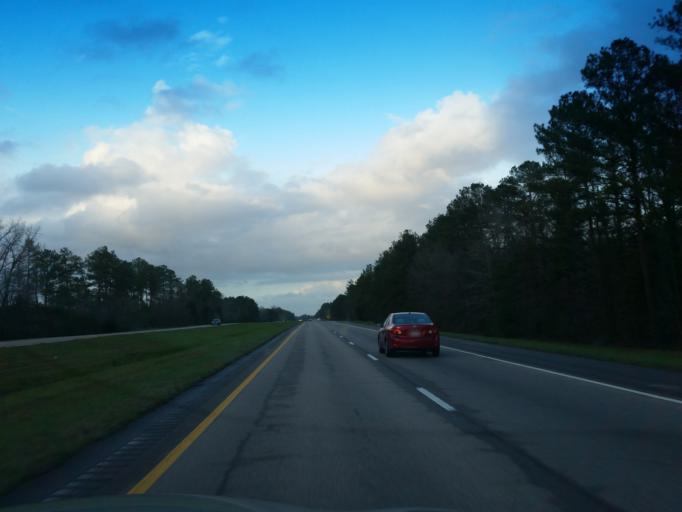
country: US
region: Mississippi
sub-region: Clarke County
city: Stonewall
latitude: 31.9938
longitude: -88.9432
